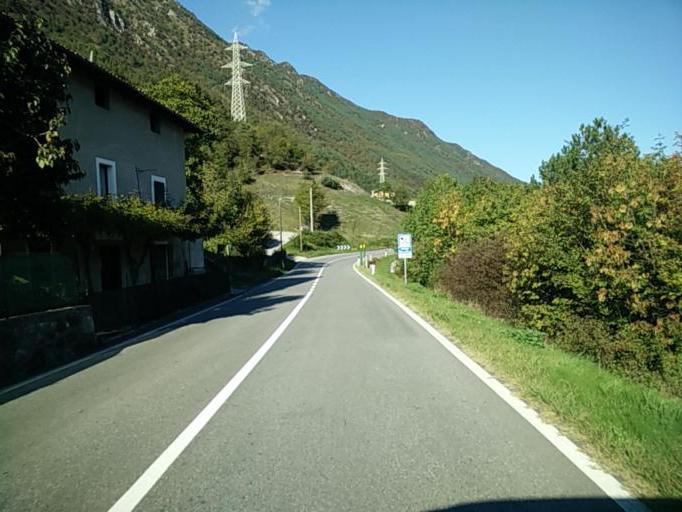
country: IT
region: Lombardy
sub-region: Provincia di Brescia
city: Ponte Caffaro
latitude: 45.8028
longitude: 10.5056
